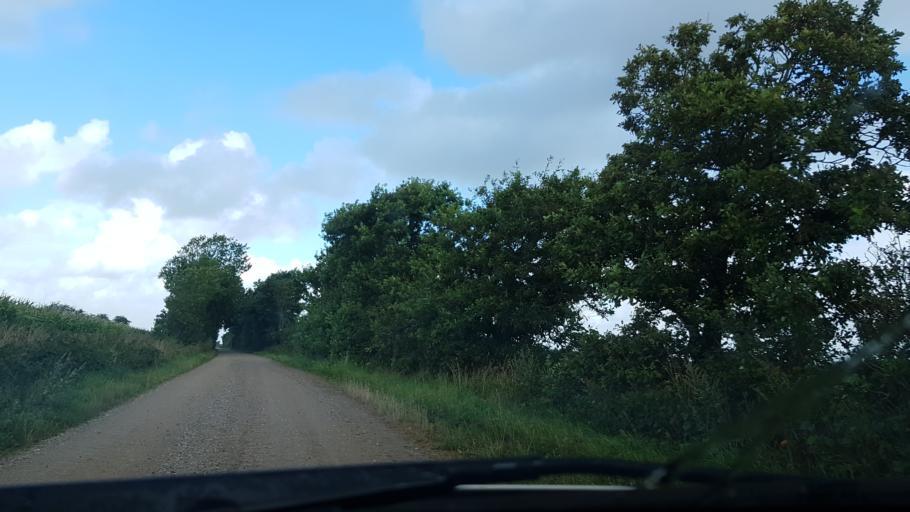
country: DK
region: South Denmark
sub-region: Tonder Kommune
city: Sherrebek
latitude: 55.2234
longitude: 8.7860
